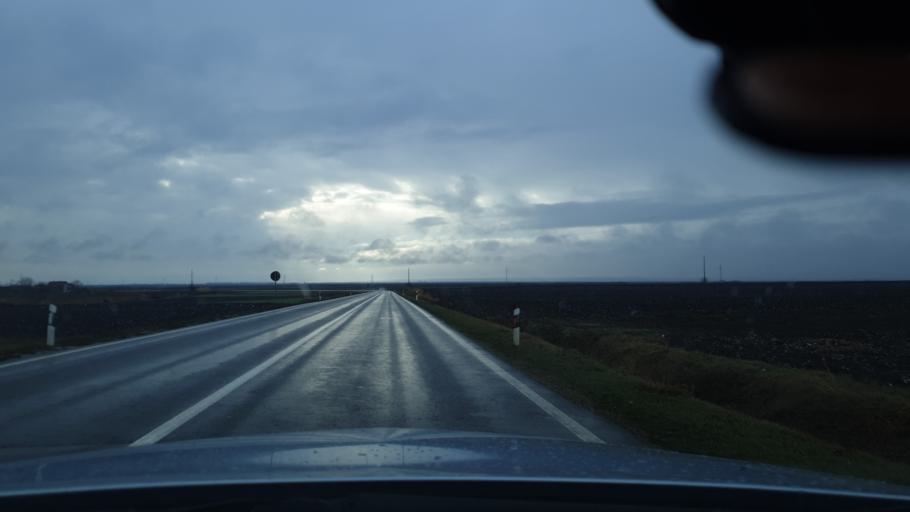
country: RS
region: Autonomna Pokrajina Vojvodina
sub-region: Juznobanatski Okrug
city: Kovin
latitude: 44.8151
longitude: 20.8556
